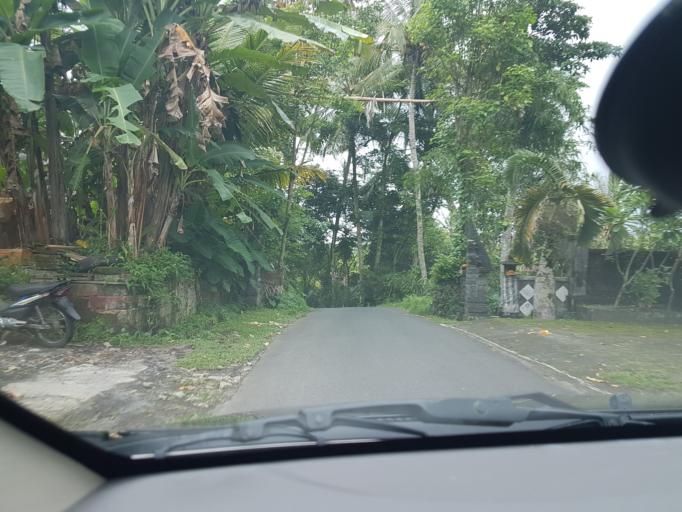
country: ID
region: Bali
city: Tegalalang
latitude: -8.4186
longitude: 115.2815
